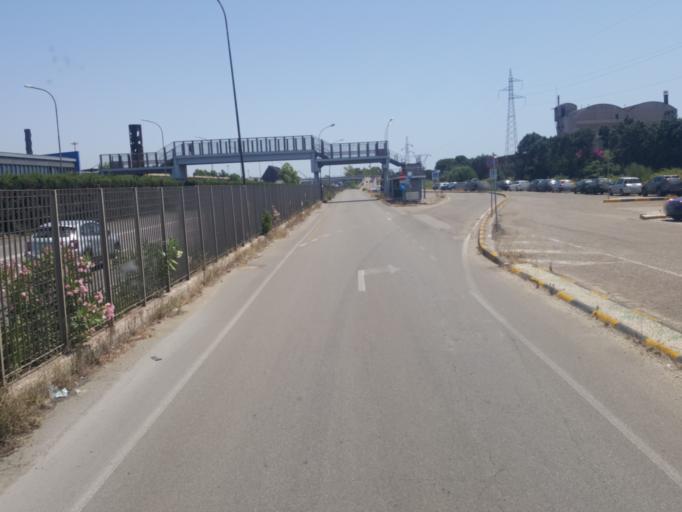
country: IT
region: Apulia
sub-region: Provincia di Taranto
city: Statte
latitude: 40.5012
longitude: 17.2002
